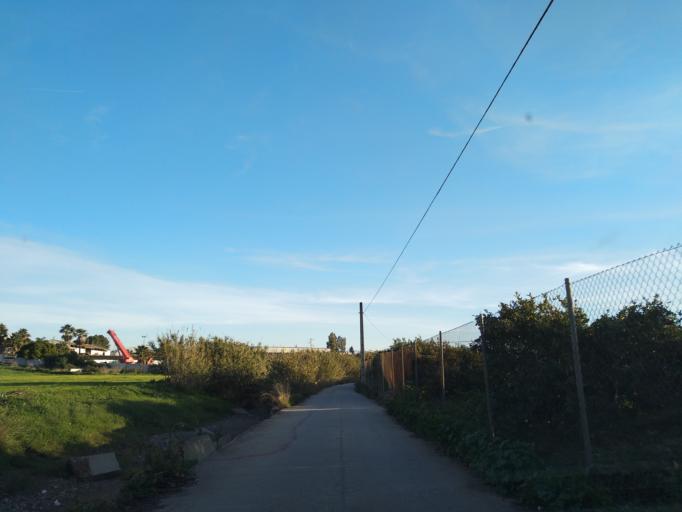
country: ES
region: Andalusia
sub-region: Provincia de Malaga
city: Estacion de Cartama
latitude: 36.7319
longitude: -4.5784
